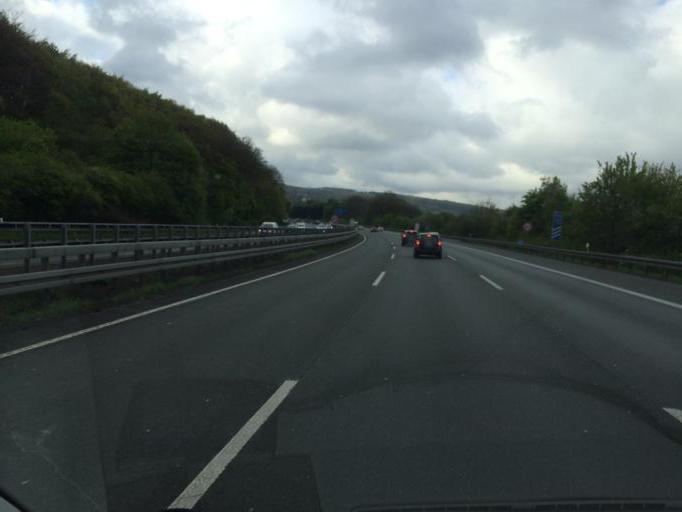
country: DE
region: North Rhine-Westphalia
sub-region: Regierungsbezirk Arnsberg
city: Schwelm
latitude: 51.2901
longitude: 7.2573
